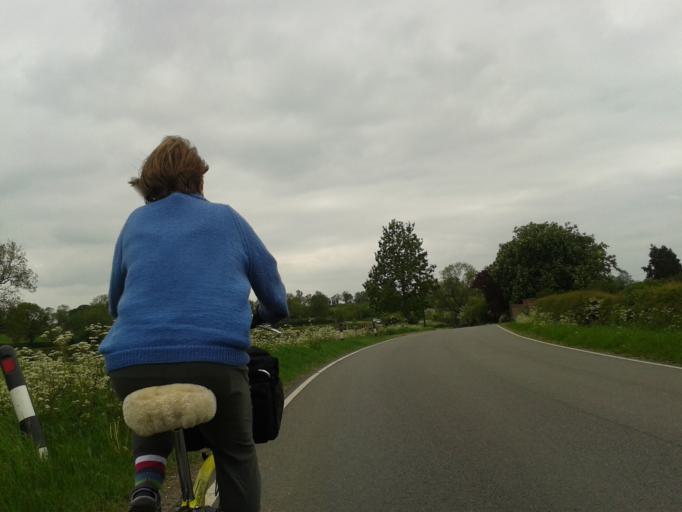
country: GB
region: England
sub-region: Leicestershire
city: Kibworth Harcourt
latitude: 52.5272
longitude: -1.0304
